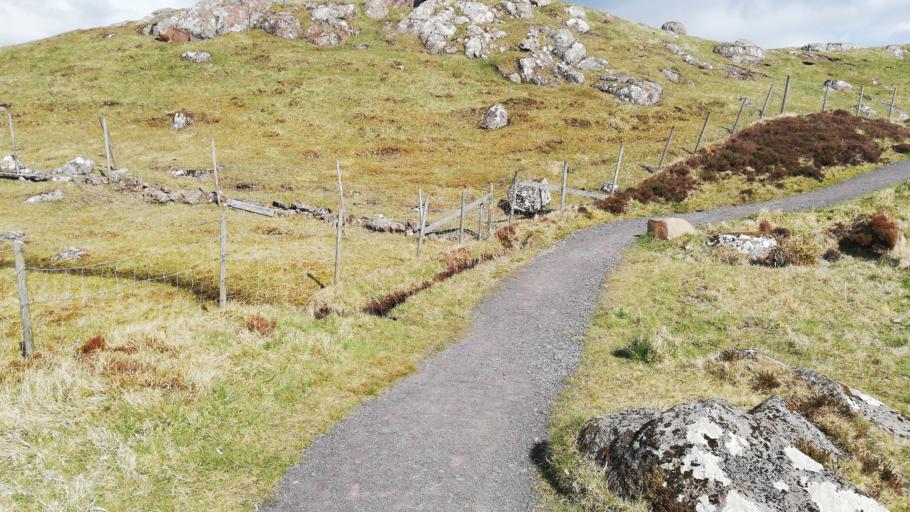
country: FO
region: Streymoy
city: Hoyvik
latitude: 62.0247
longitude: -6.7769
